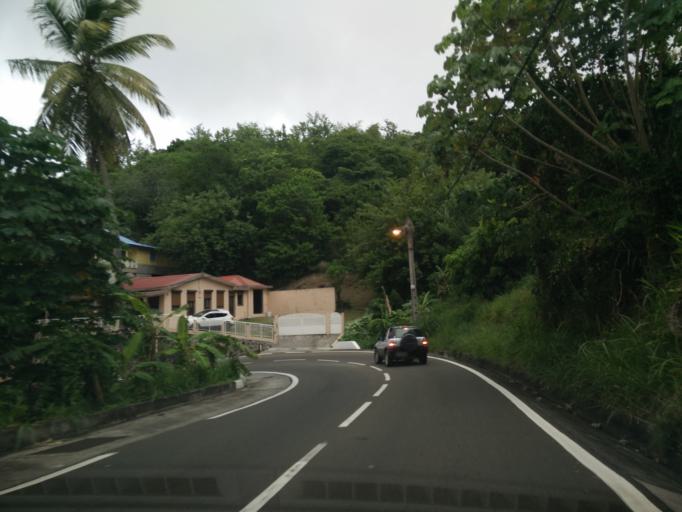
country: MQ
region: Martinique
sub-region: Martinique
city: Le Marin
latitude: 14.4955
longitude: -60.8567
